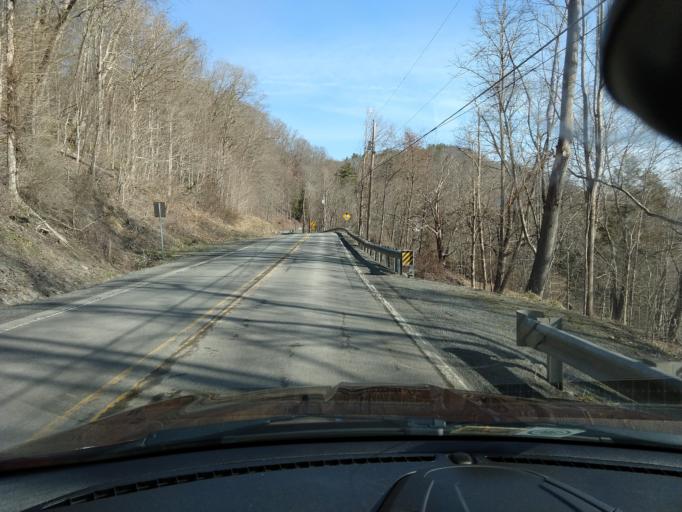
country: US
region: West Virginia
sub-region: Pocahontas County
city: Marlinton
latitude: 38.2192
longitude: -80.1014
